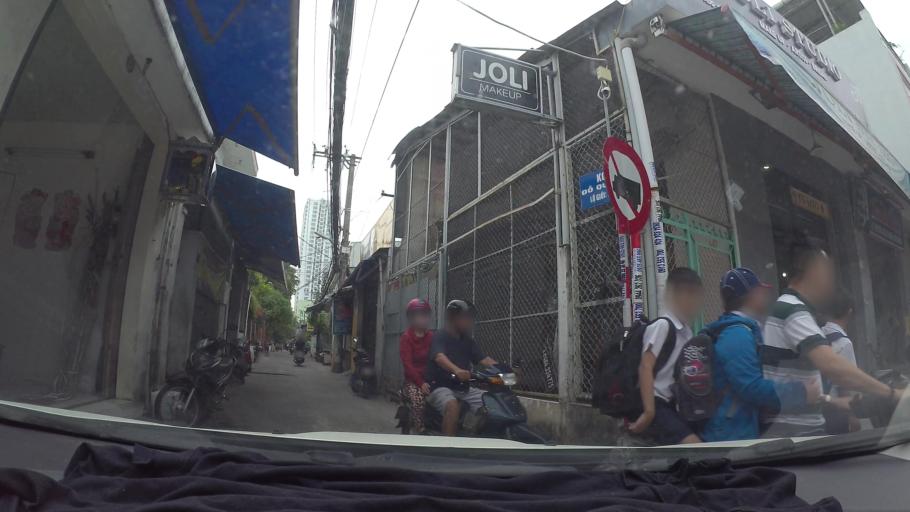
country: VN
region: Da Nang
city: Da Nang
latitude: 16.0629
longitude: 108.2135
